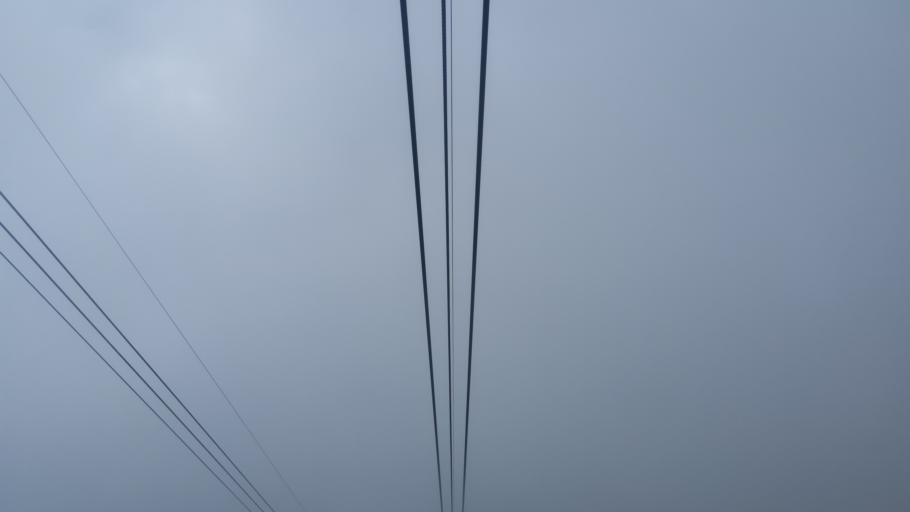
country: IT
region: Trentino-Alto Adige
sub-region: Provincia di Trento
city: Siror
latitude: 46.2664
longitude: 11.8307
